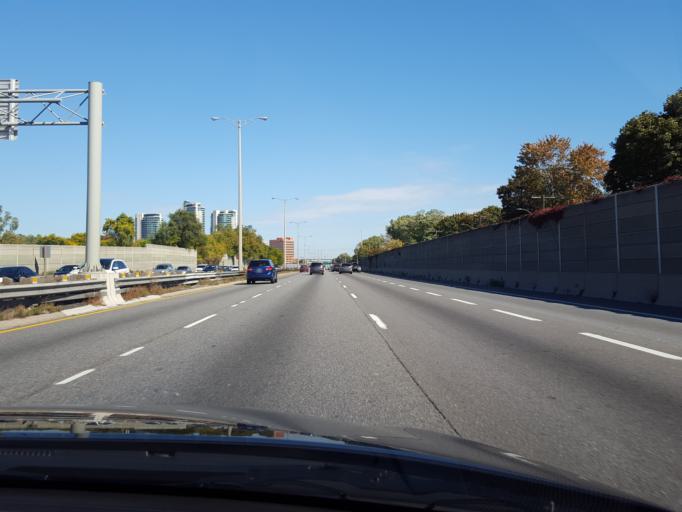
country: CA
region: Ontario
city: Etobicoke
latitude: 43.6006
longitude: -79.5644
